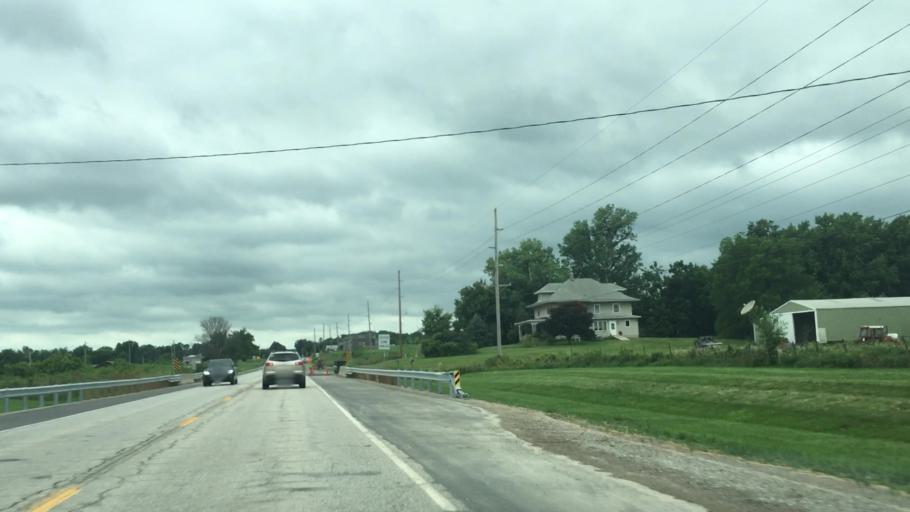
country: US
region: Iowa
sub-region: Johnson County
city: Tiffin
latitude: 41.7062
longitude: -91.6505
